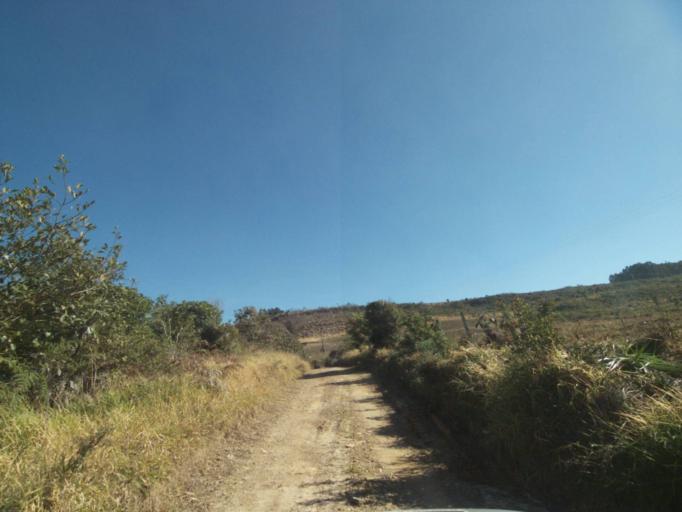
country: BR
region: Parana
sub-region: Tibagi
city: Tibagi
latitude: -24.5761
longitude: -50.4780
